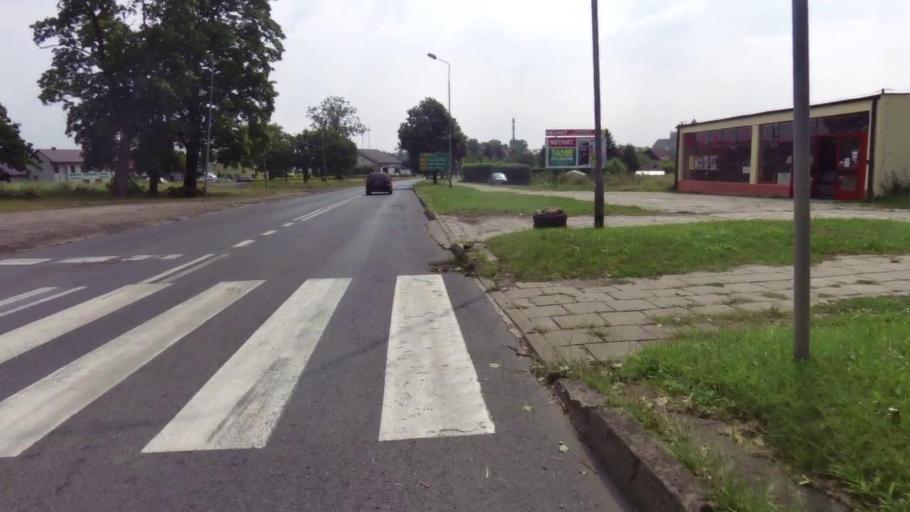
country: PL
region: West Pomeranian Voivodeship
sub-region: Powiat choszczenski
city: Choszczno
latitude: 53.1747
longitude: 15.4148
